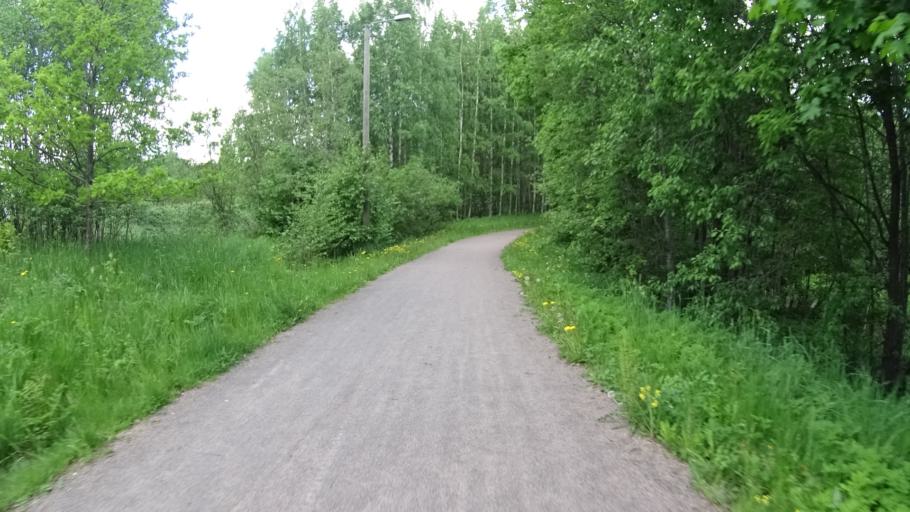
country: FI
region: Uusimaa
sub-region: Helsinki
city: Espoo
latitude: 60.2206
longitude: 24.6617
